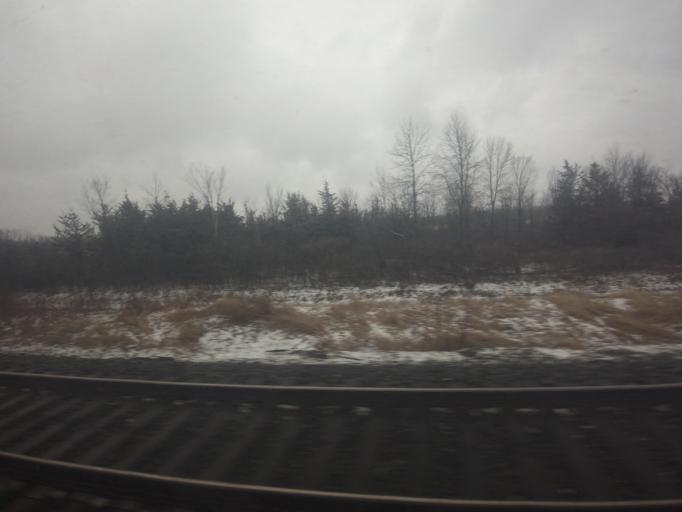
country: CA
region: Ontario
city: Deseronto
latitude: 44.2143
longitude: -77.1798
